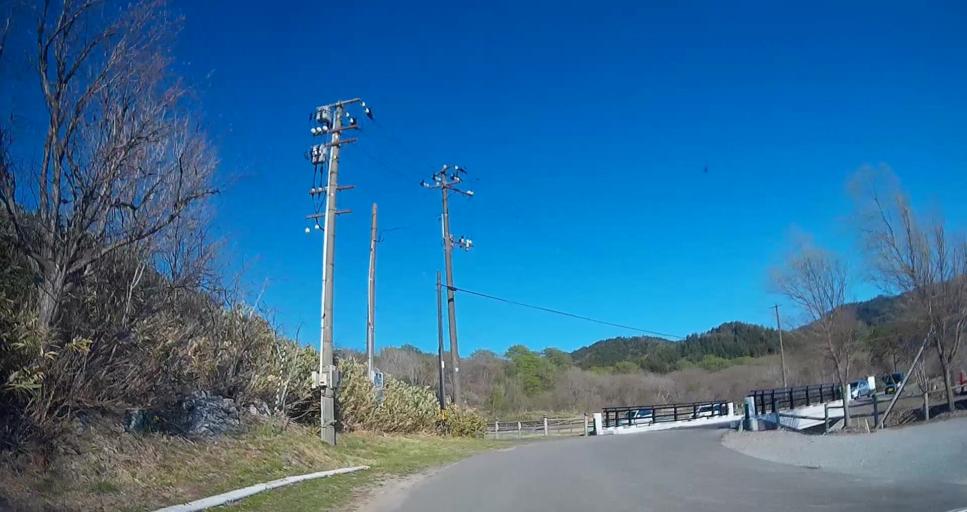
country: JP
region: Aomori
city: Mutsu
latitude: 41.3264
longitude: 141.0960
